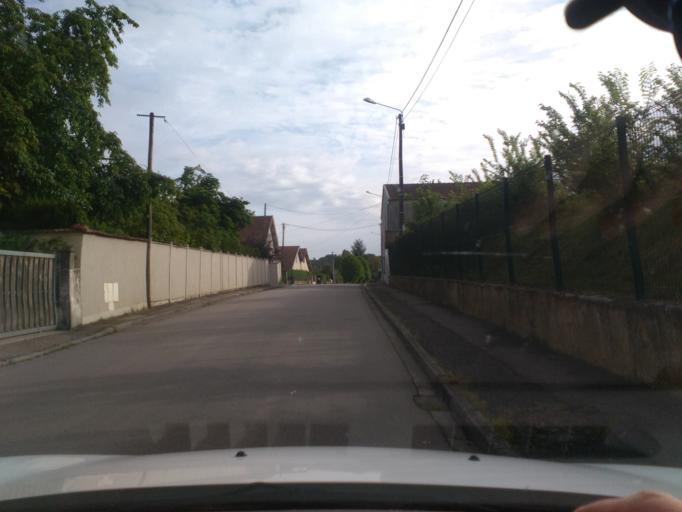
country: FR
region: Lorraine
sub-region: Departement des Vosges
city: Mirecourt
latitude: 48.3029
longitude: 6.1401
